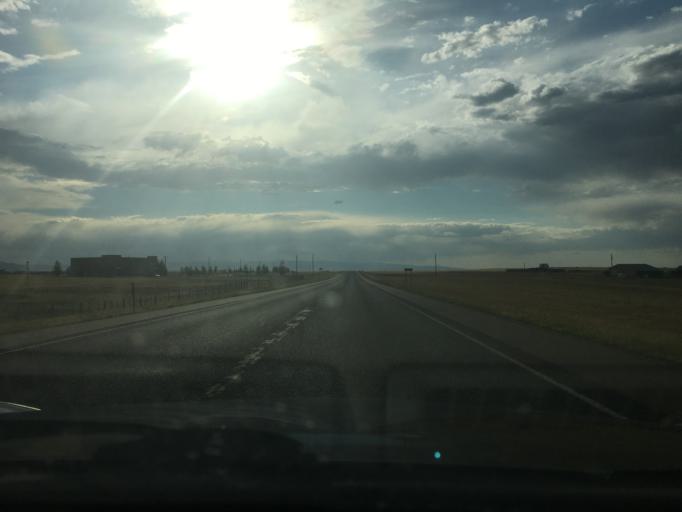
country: US
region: Wyoming
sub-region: Albany County
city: Laramie
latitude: 41.3223
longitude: -105.6613
